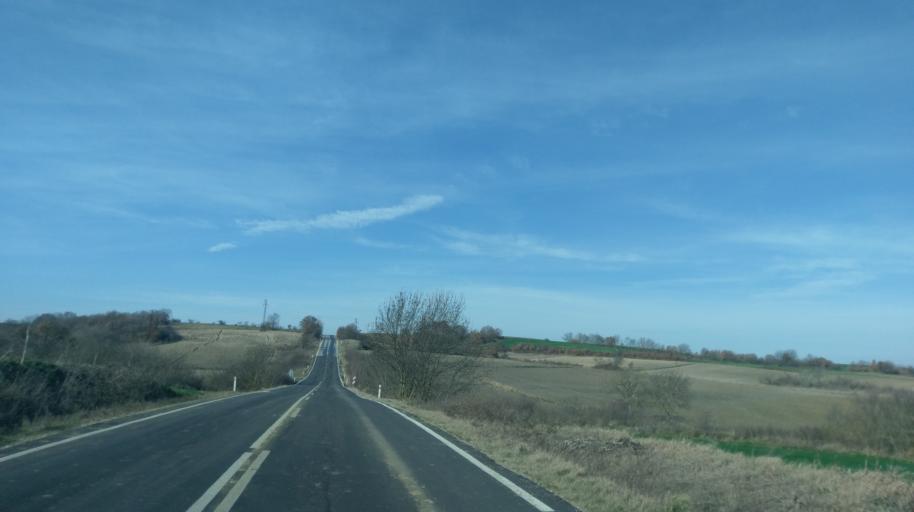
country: TR
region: Edirne
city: Copkoy
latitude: 41.2733
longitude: 26.7882
